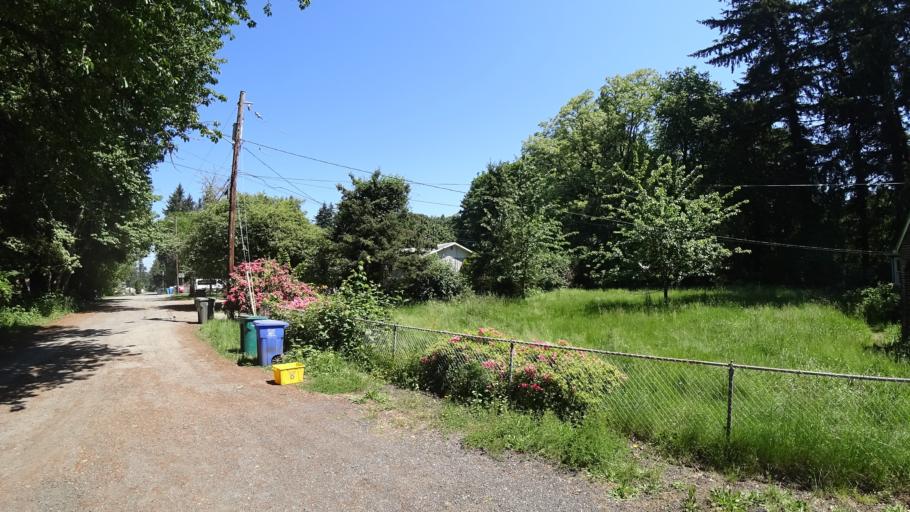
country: US
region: Oregon
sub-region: Clackamas County
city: Happy Valley
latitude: 45.4746
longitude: -122.5198
